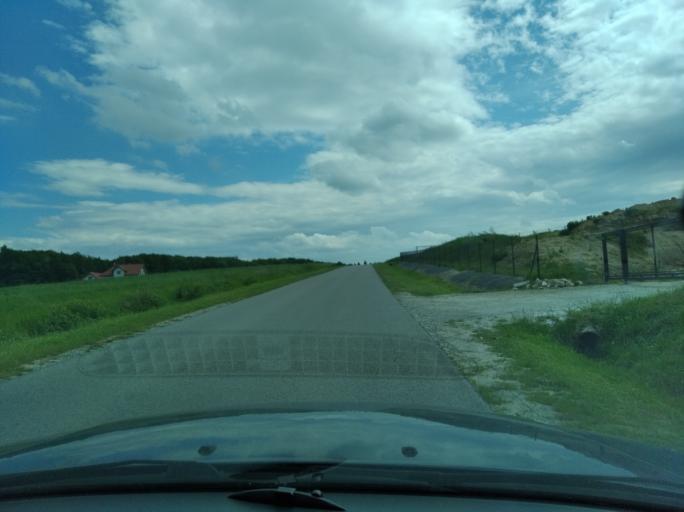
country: PL
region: Subcarpathian Voivodeship
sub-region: Powiat ropczycko-sedziszowski
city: Ropczyce
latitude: 50.0232
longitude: 21.6046
